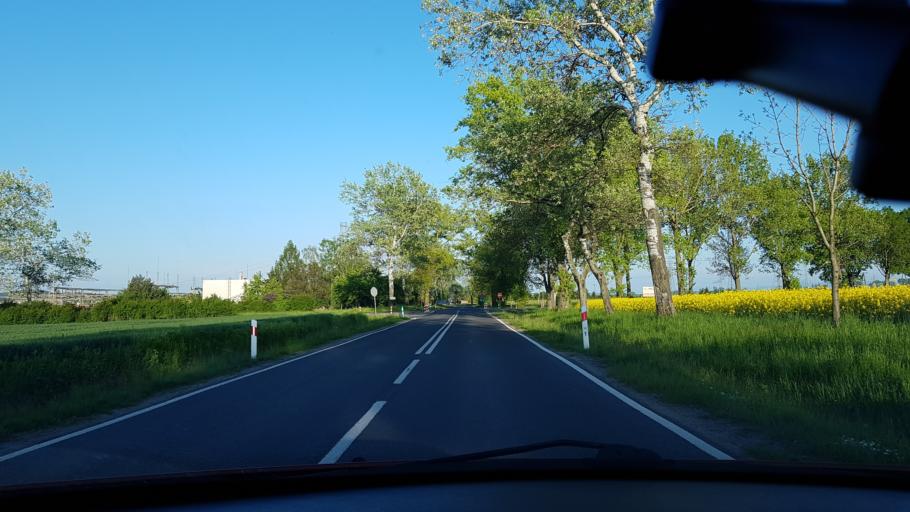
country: PL
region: Lower Silesian Voivodeship
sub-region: Powiat zabkowicki
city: Zabkowice Slaskie
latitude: 50.5938
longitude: 16.7852
